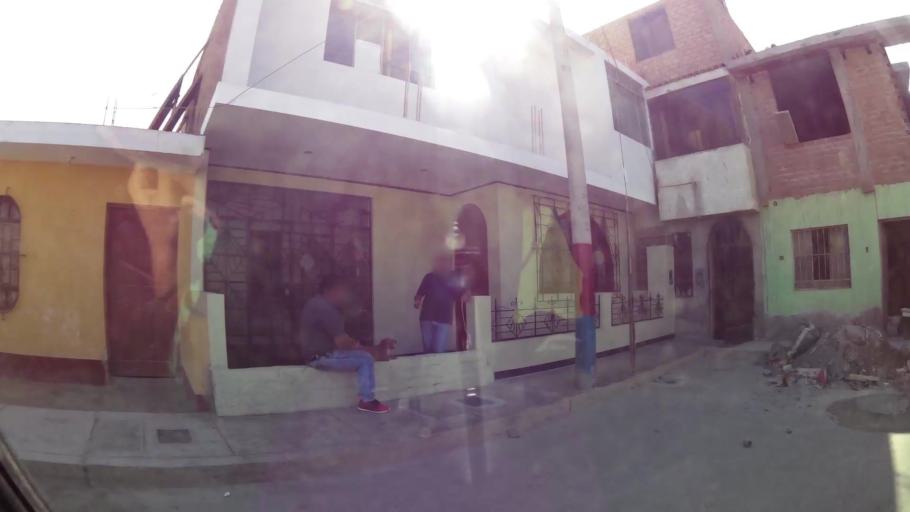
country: PE
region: Ancash
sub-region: Provincia de Huarmey
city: Huarmey
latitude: -10.0695
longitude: -78.1493
